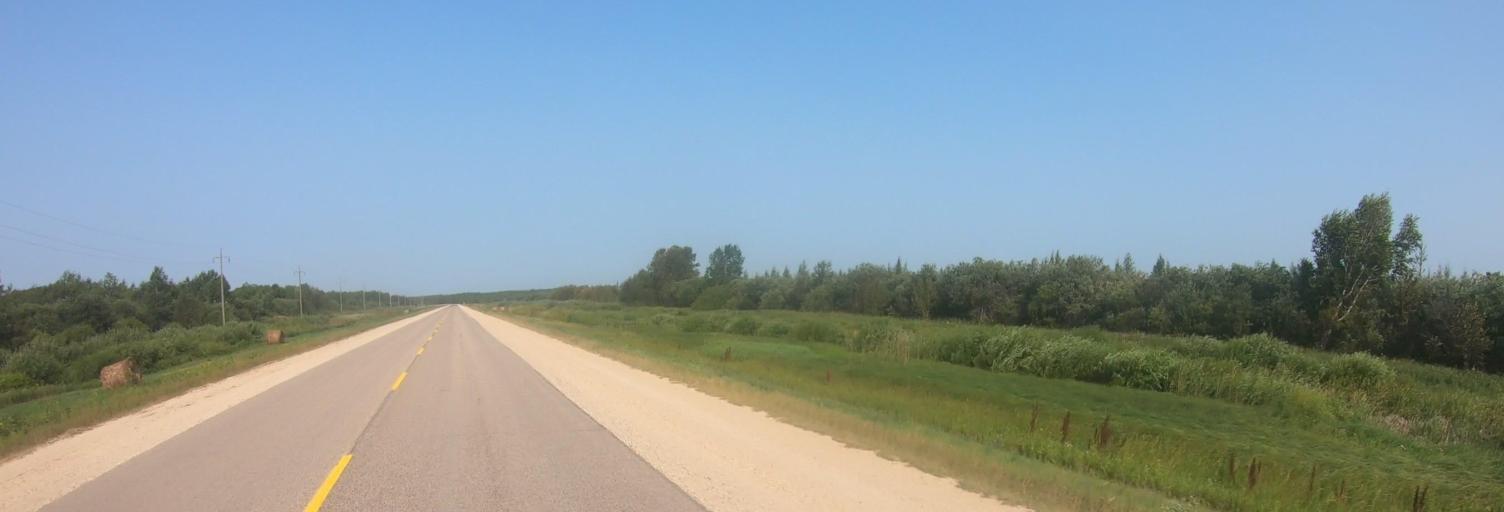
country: US
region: Minnesota
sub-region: Roseau County
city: Warroad
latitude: 49.0196
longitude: -95.5504
